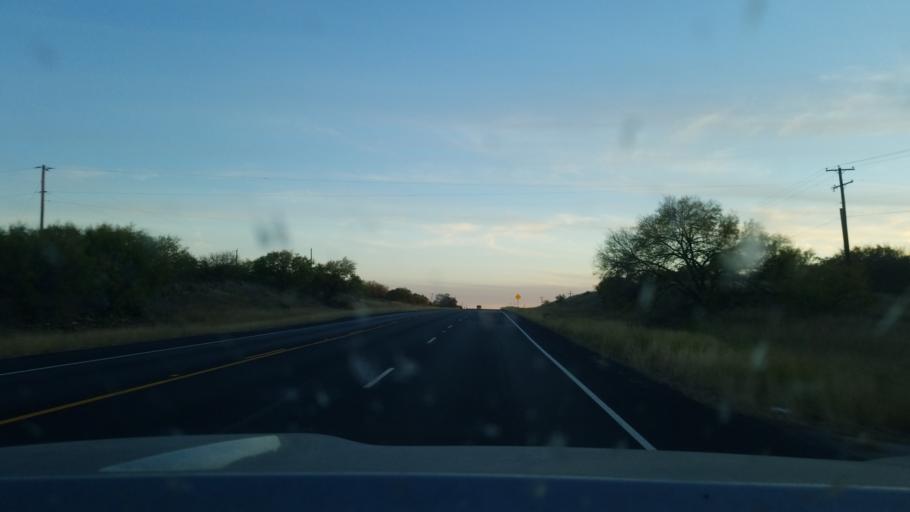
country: US
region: Texas
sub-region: Stephens County
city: Breckenridge
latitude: 32.6830
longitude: -98.9028
